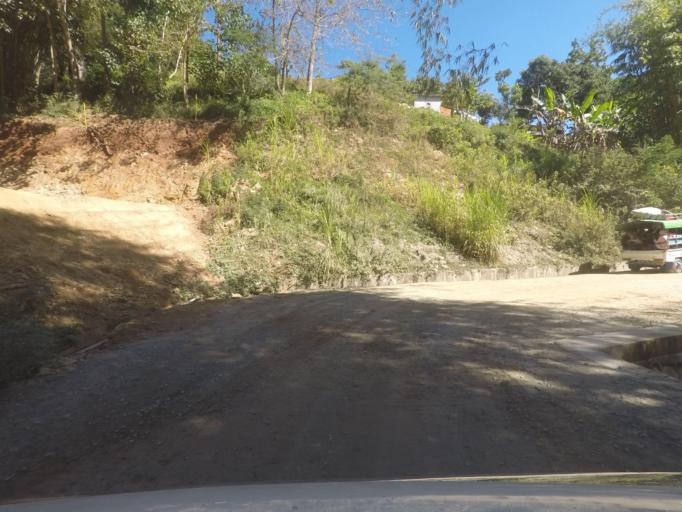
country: TL
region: Ermera
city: Gleno
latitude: -8.7506
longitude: 125.3959
